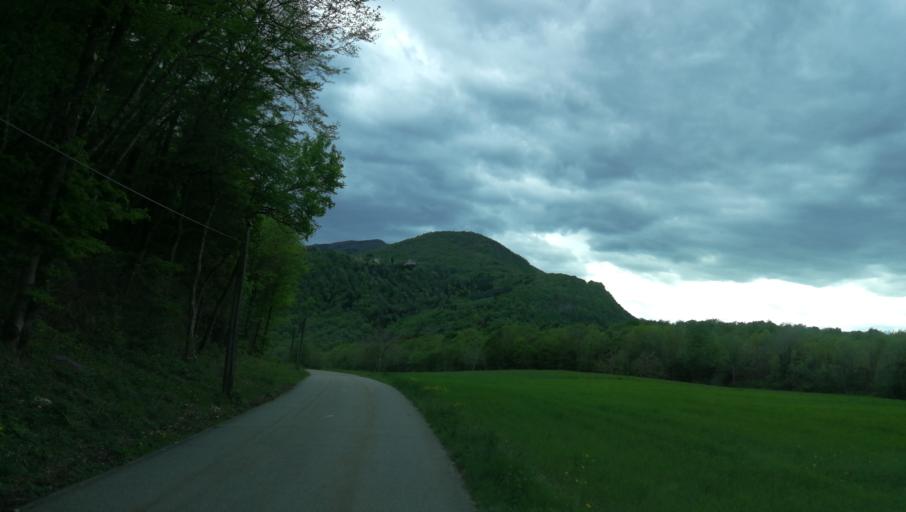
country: FR
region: Rhone-Alpes
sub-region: Departement de la Savoie
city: Chatillon
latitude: 45.7720
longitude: 5.8209
